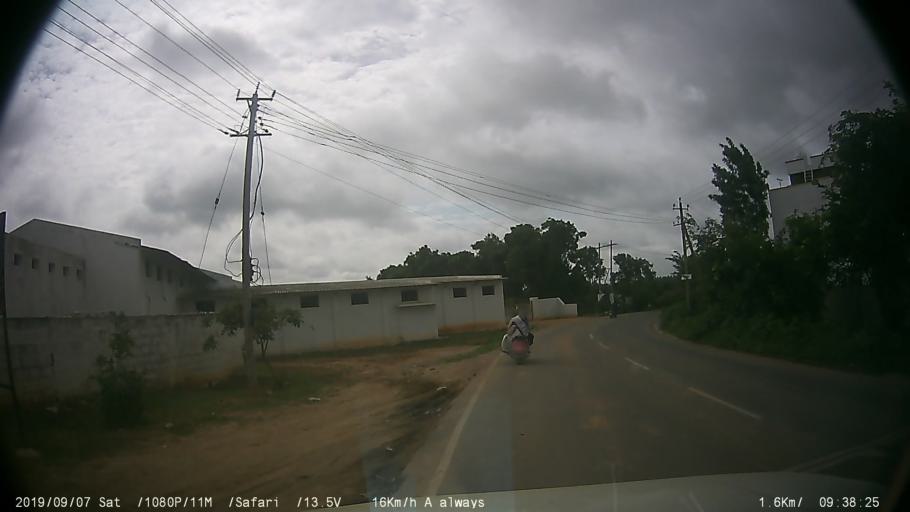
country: IN
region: Karnataka
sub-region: Bangalore Urban
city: Anekal
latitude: 12.8177
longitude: 77.6278
